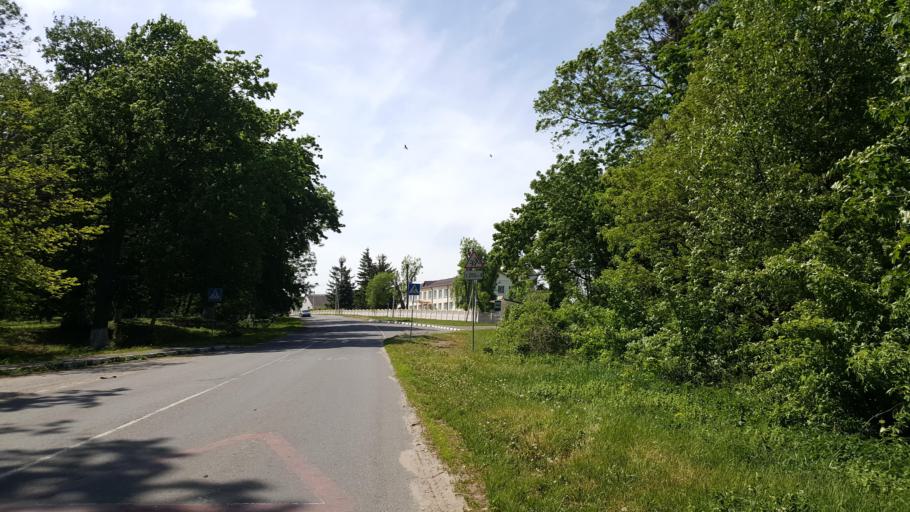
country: BY
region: Brest
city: Charnawchytsy
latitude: 52.2037
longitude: 23.6899
